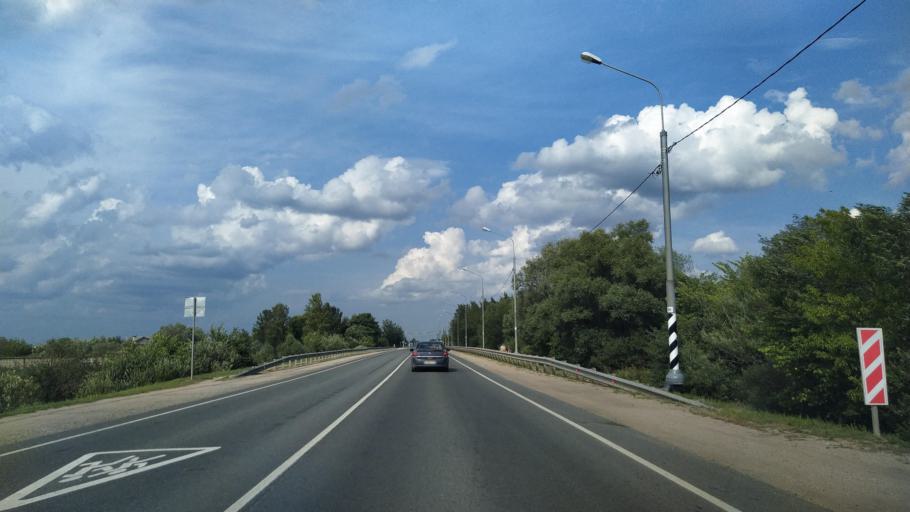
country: RU
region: Novgorod
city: Shimsk
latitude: 58.2136
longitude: 30.7273
